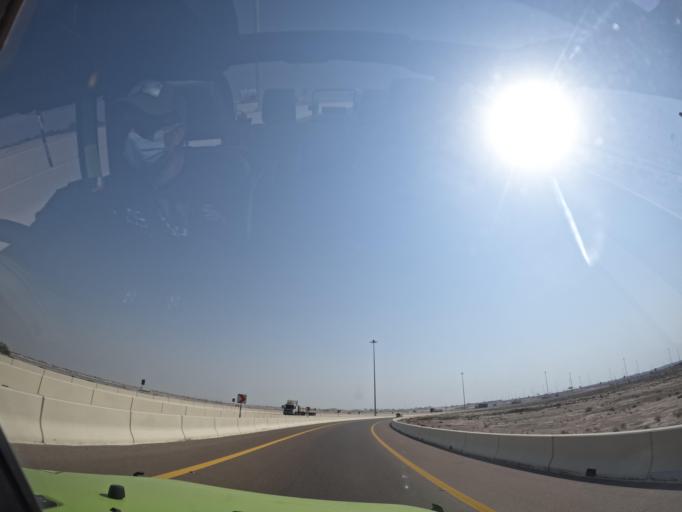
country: AE
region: Abu Dhabi
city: Abu Dhabi
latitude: 24.4073
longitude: 54.6768
